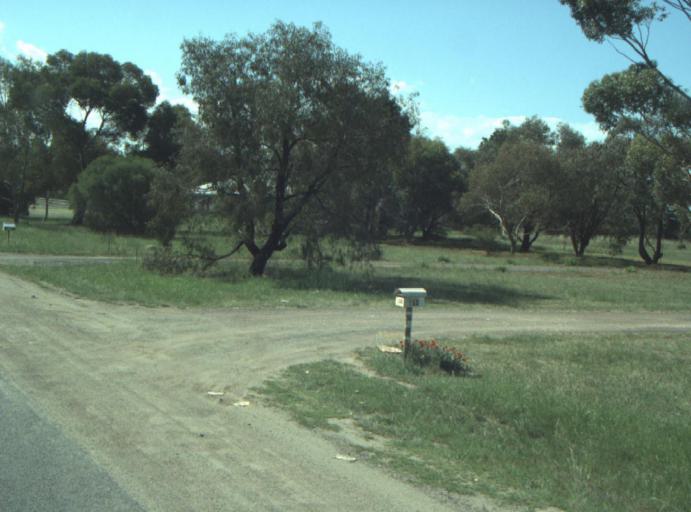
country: AU
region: Victoria
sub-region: Greater Geelong
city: Lara
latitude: -38.0120
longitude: 144.3860
